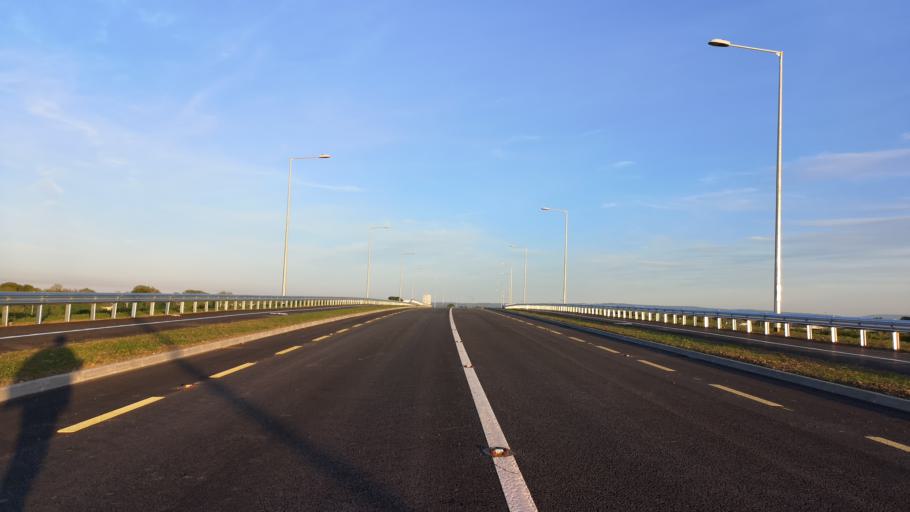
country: IE
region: Connaught
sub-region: County Galway
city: Athenry
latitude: 53.2970
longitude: -8.7622
